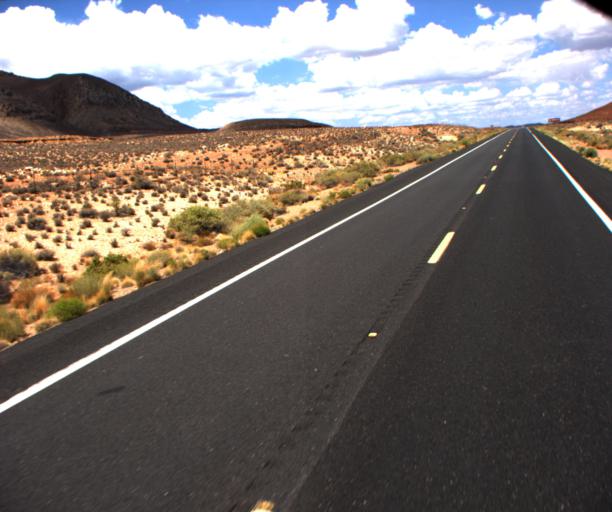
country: US
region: Arizona
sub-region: Coconino County
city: Tuba City
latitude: 35.9013
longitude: -111.5445
